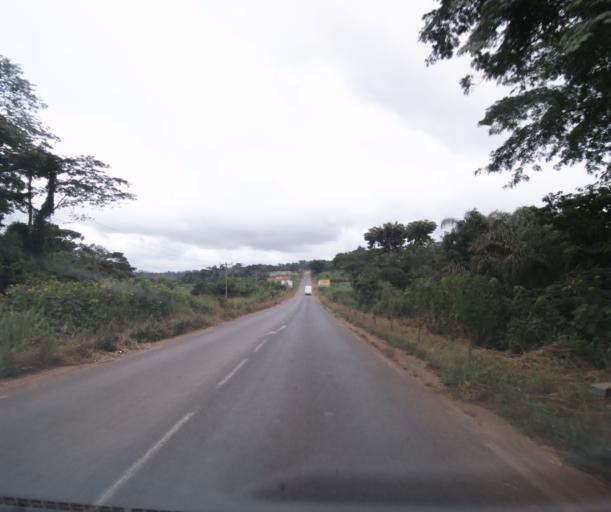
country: CM
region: Centre
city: Mbankomo
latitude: 3.7851
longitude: 11.4555
